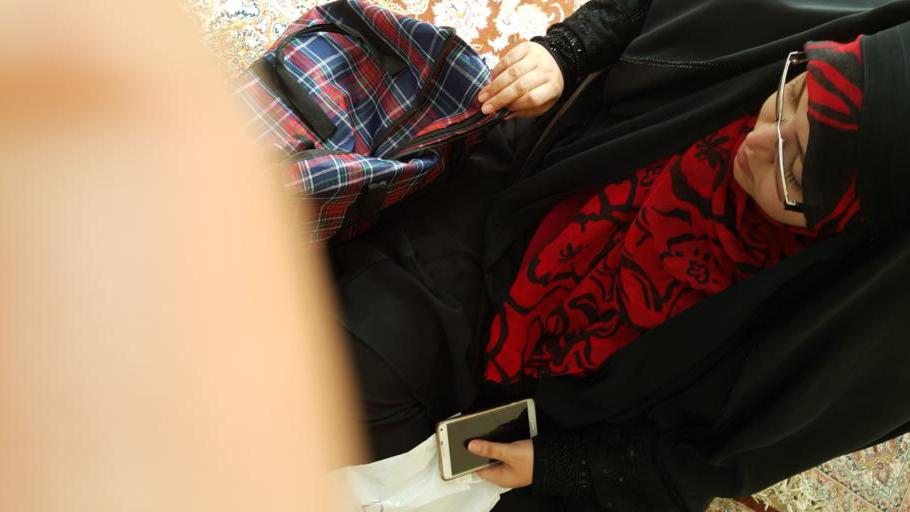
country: IQ
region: An Najaf
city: An Najaf
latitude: 31.9967
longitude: 44.3145
